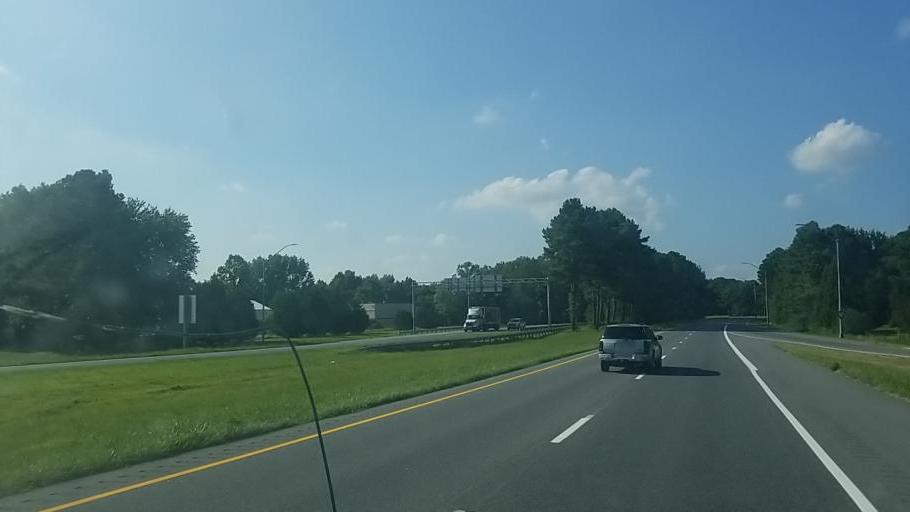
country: US
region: Maryland
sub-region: Worcester County
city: Berlin
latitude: 38.3454
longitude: -75.2141
